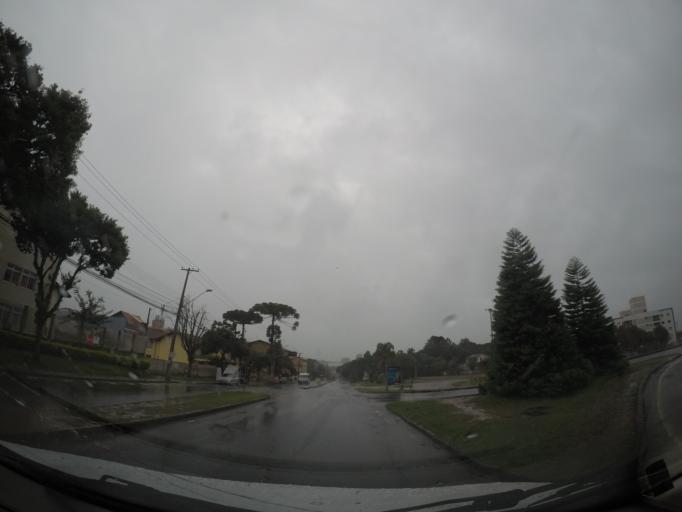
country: BR
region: Parana
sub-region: Curitiba
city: Curitiba
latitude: -25.4500
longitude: -49.3530
